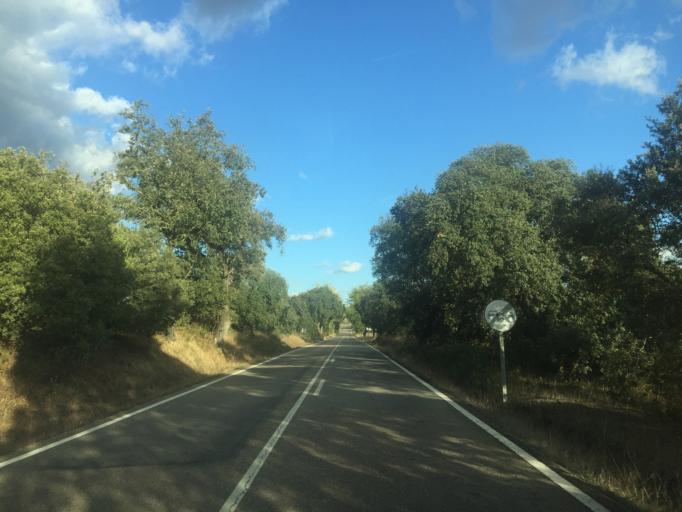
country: PT
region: Portalegre
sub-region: Alter do Chao
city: Alter do Chao
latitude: 39.2037
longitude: -7.7498
